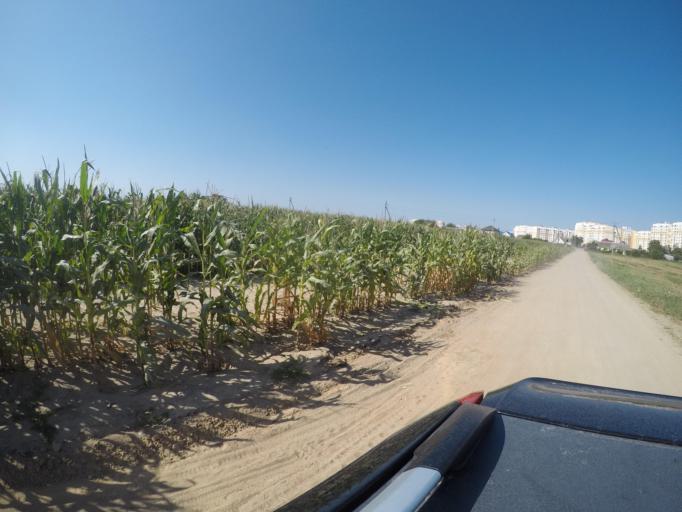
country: BY
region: Grodnenskaya
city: Hrodna
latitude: 53.7097
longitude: 23.8724
